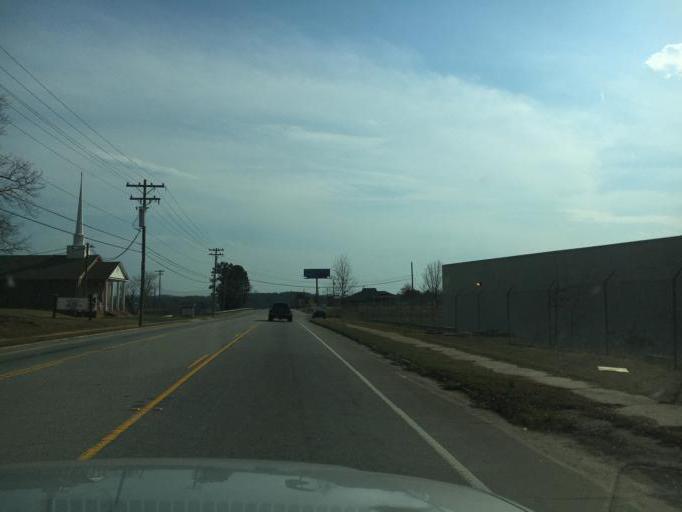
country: US
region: South Carolina
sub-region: Spartanburg County
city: Mayo
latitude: 35.1399
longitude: -81.8609
